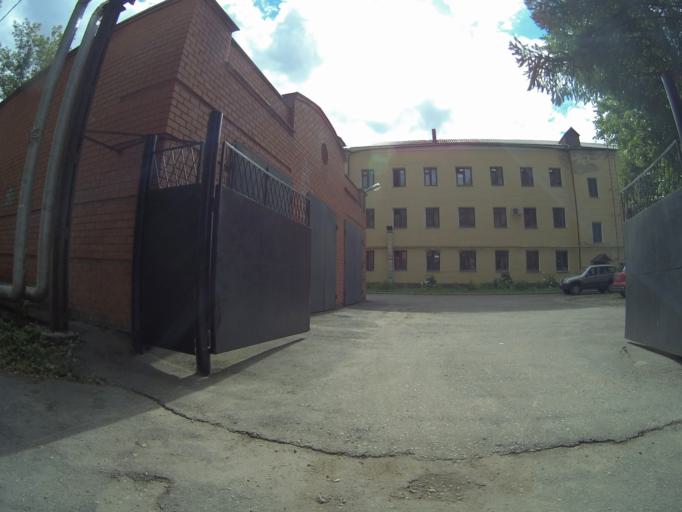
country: RU
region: Vladimir
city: Vladimir
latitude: 56.1429
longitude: 40.4226
